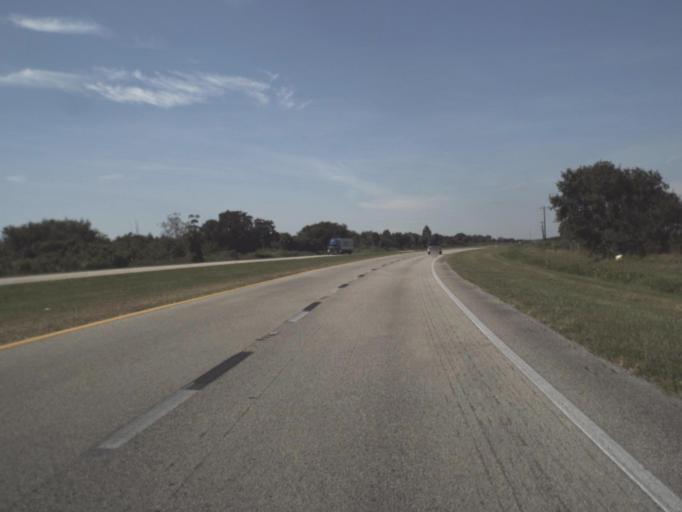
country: US
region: Florida
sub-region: Glades County
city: Moore Haven
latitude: 26.9021
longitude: -81.2512
